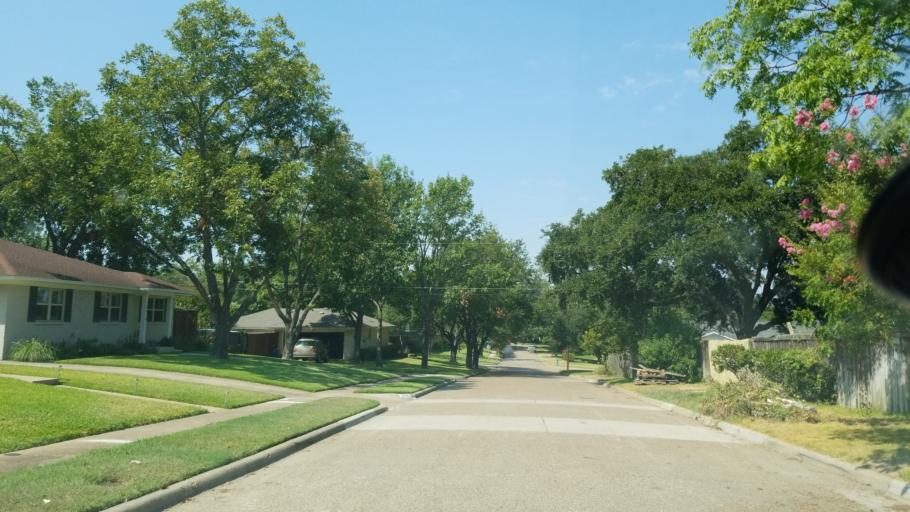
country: US
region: Texas
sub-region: Dallas County
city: Richardson
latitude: 32.8760
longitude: -96.7117
